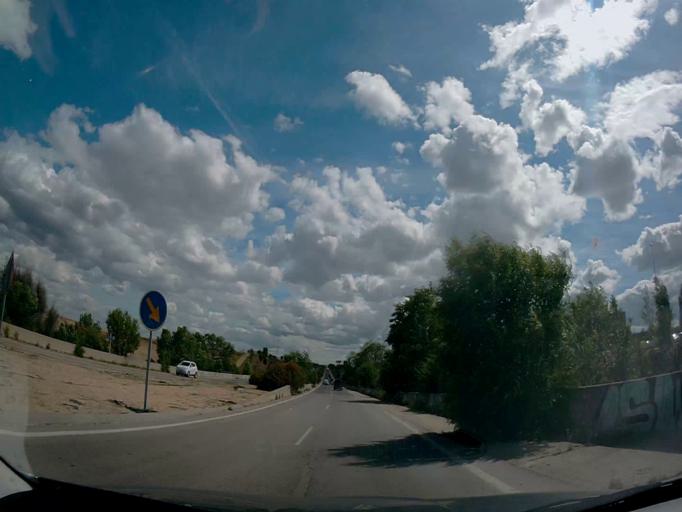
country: ES
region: Madrid
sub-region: Provincia de Madrid
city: San Sebastian de los Reyes
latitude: 40.5604
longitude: -3.6086
